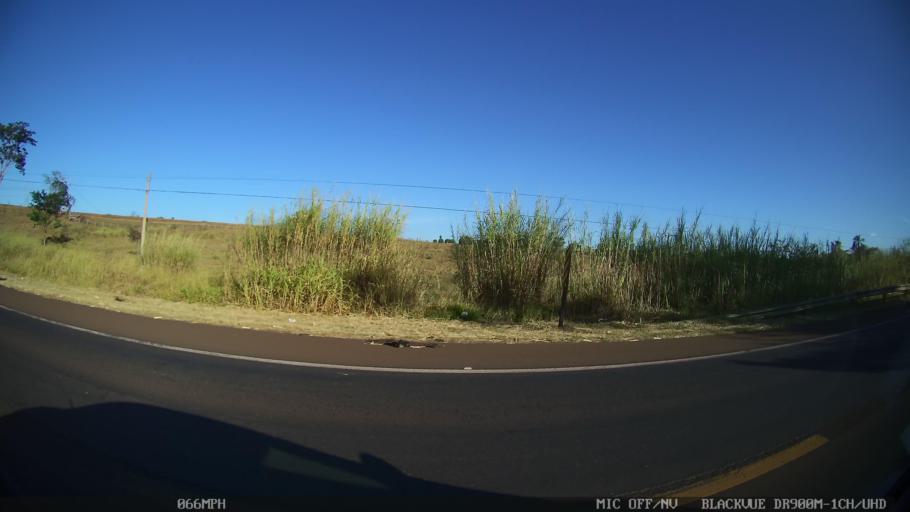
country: BR
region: Sao Paulo
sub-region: Olimpia
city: Olimpia
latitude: -20.7086
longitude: -48.9674
